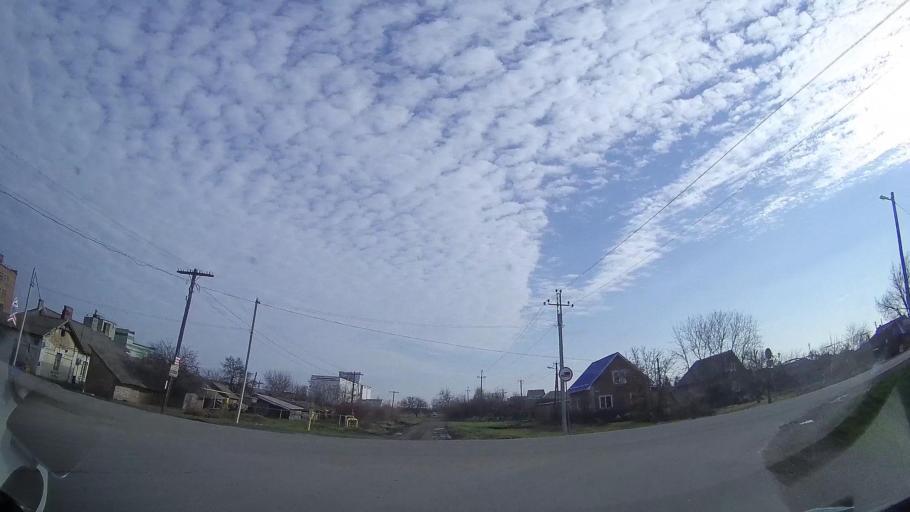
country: RU
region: Rostov
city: Tselina
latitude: 46.5375
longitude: 41.0508
